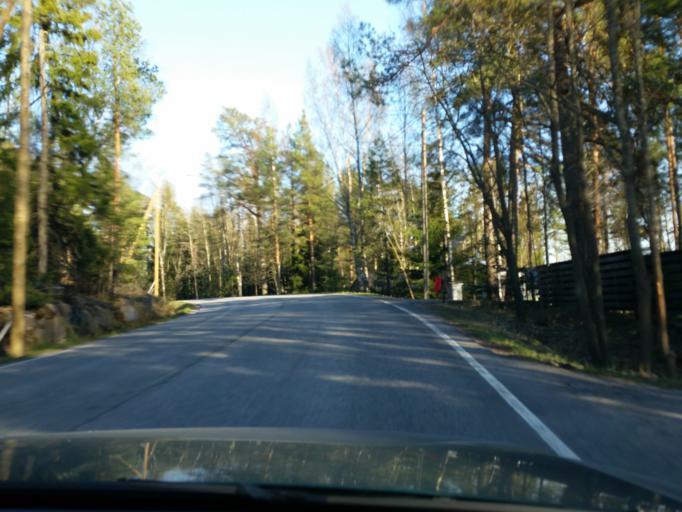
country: FI
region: Uusimaa
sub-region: Helsinki
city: Kirkkonummi
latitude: 60.1207
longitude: 24.5340
